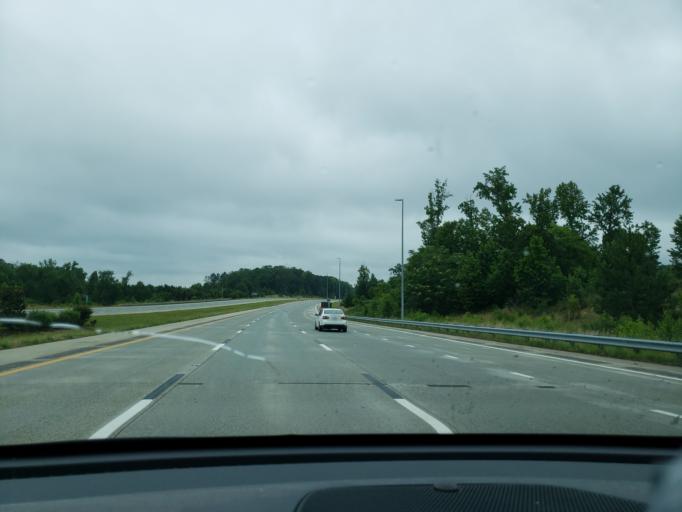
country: US
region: North Carolina
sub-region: Wake County
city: Green Level
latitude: 35.7555
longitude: -78.8916
